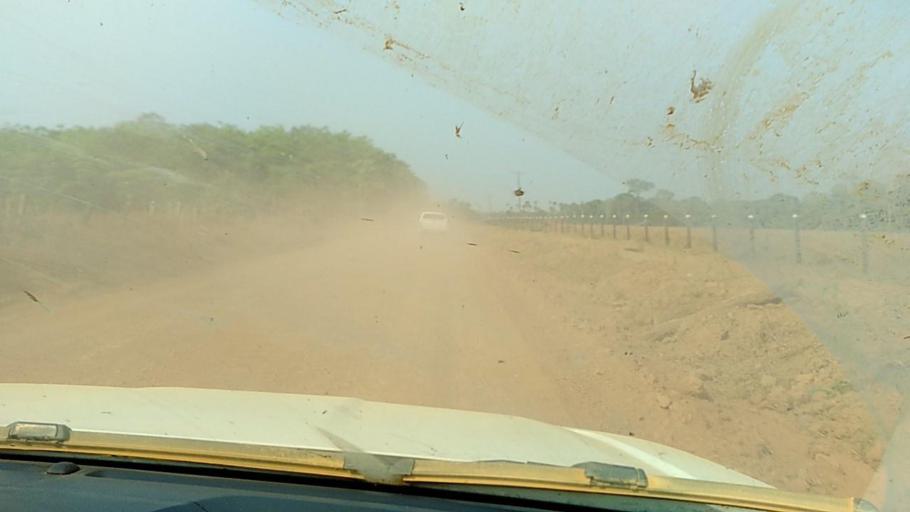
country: BR
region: Rondonia
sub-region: Porto Velho
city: Porto Velho
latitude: -8.7841
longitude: -64.0900
